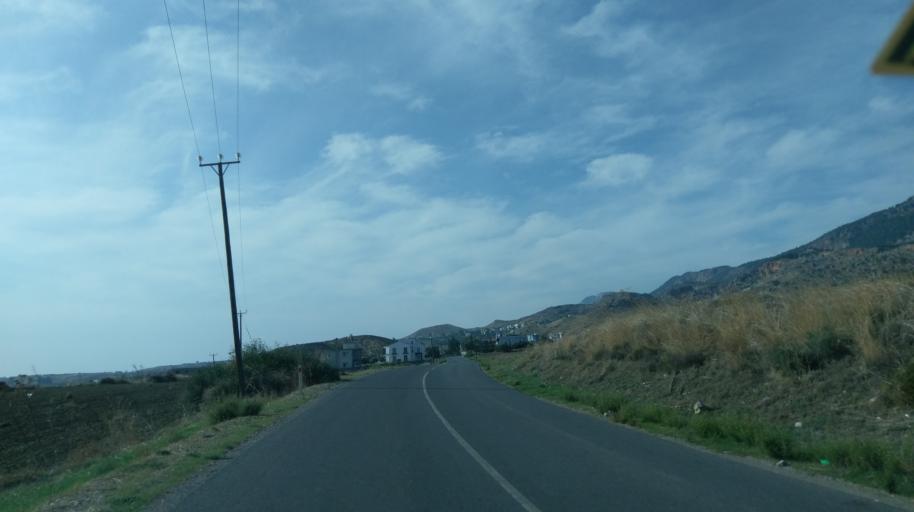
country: CY
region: Keryneia
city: Kyrenia
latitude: 35.2833
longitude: 33.2595
